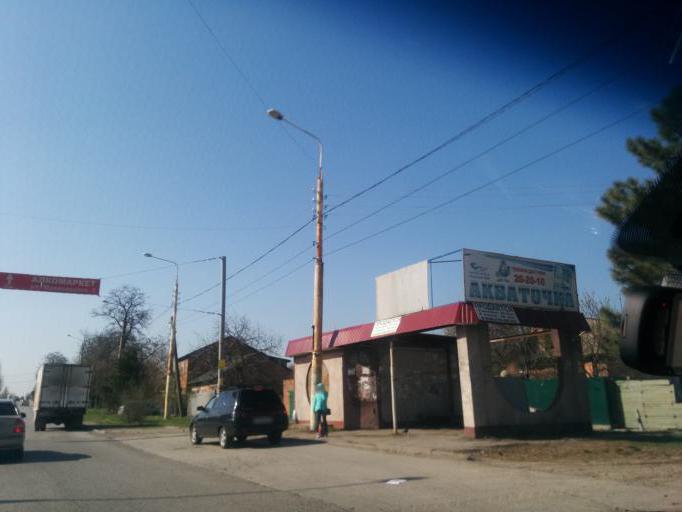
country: RU
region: Rostov
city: Shakhty
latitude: 47.6984
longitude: 40.2079
